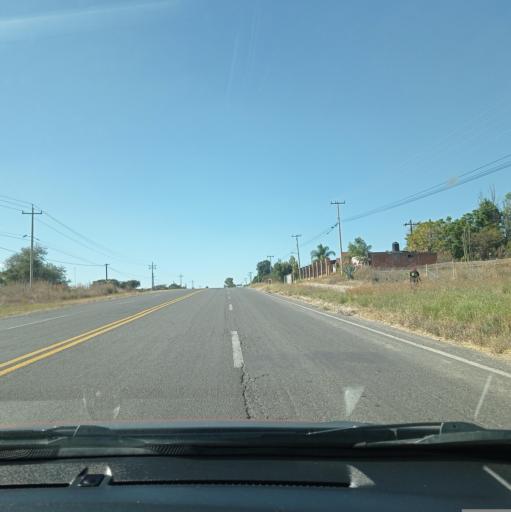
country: MX
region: Jalisco
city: San Miguel el Alto
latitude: 21.0243
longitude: -102.3658
